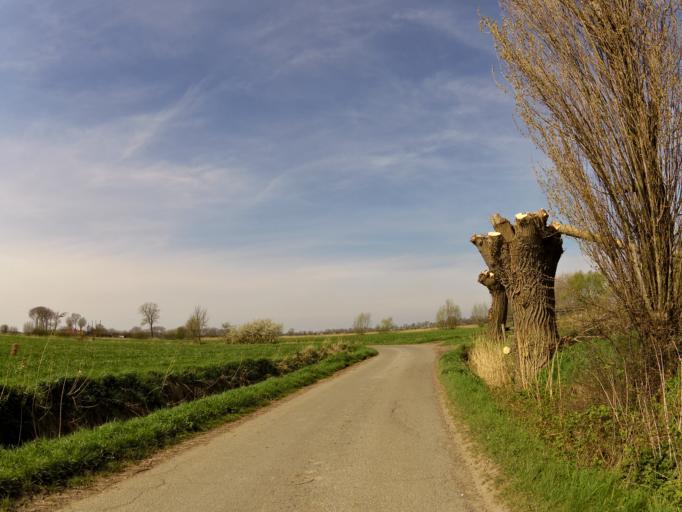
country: BE
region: Flanders
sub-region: Provincie West-Vlaanderen
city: Oudenburg
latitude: 51.1926
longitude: 3.0388
